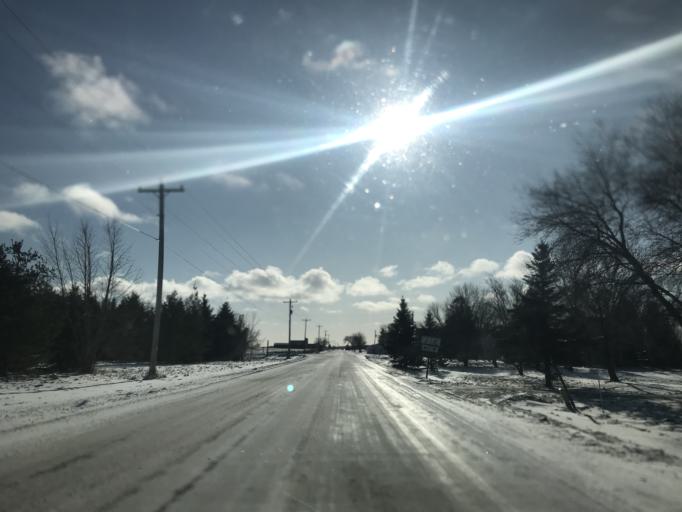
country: US
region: Wisconsin
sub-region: Kewaunee County
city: Luxemburg
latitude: 44.6989
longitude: -87.6205
